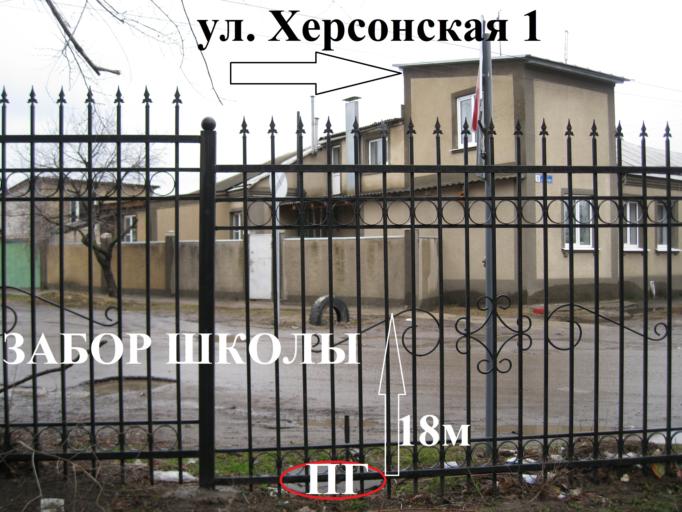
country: RU
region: Voronezj
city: Voronezh
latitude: 51.6320
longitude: 39.1834
